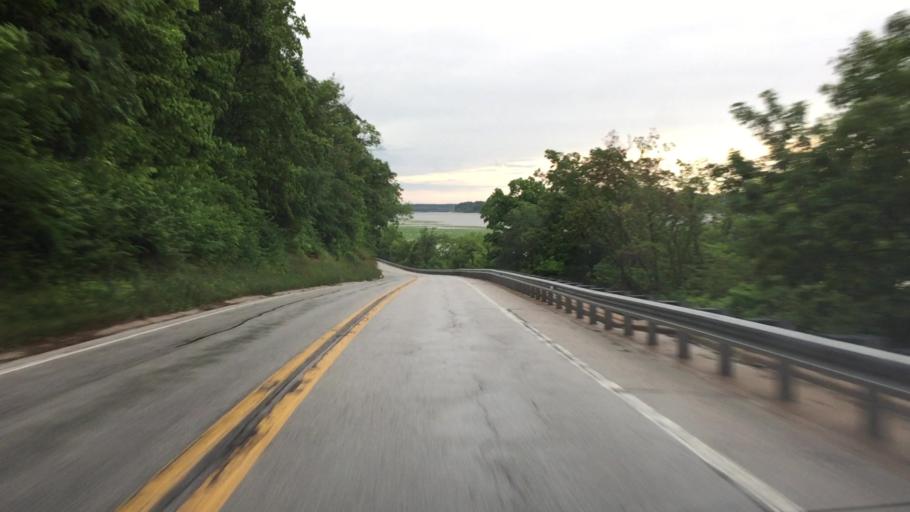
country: US
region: Iowa
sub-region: Lee County
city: Keokuk
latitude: 40.4402
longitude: -91.3716
